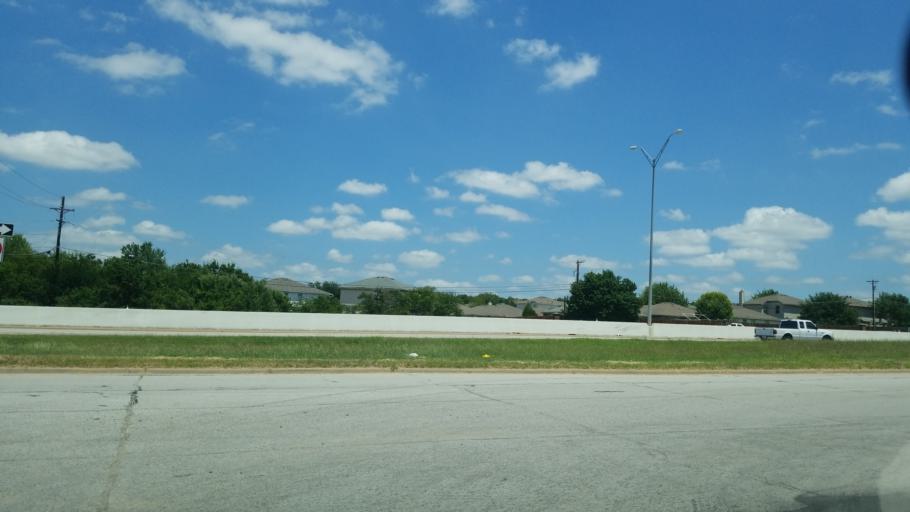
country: US
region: Texas
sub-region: Dallas County
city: Hutchins
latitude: 32.7356
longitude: -96.7154
